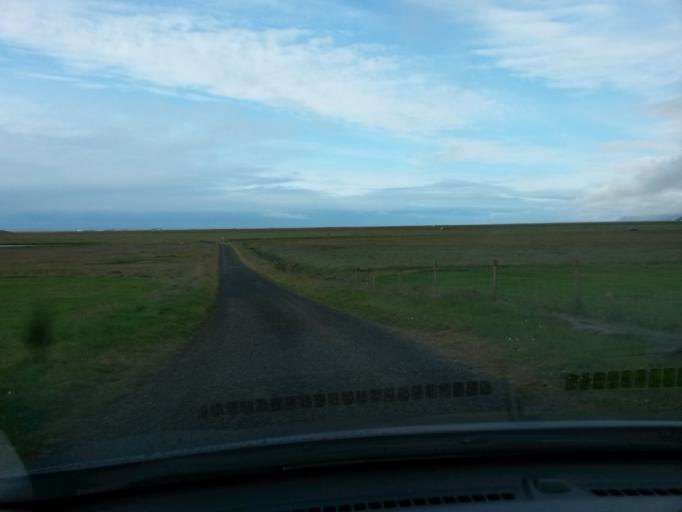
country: IS
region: South
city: Vestmannaeyjar
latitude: 63.4378
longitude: -19.1904
